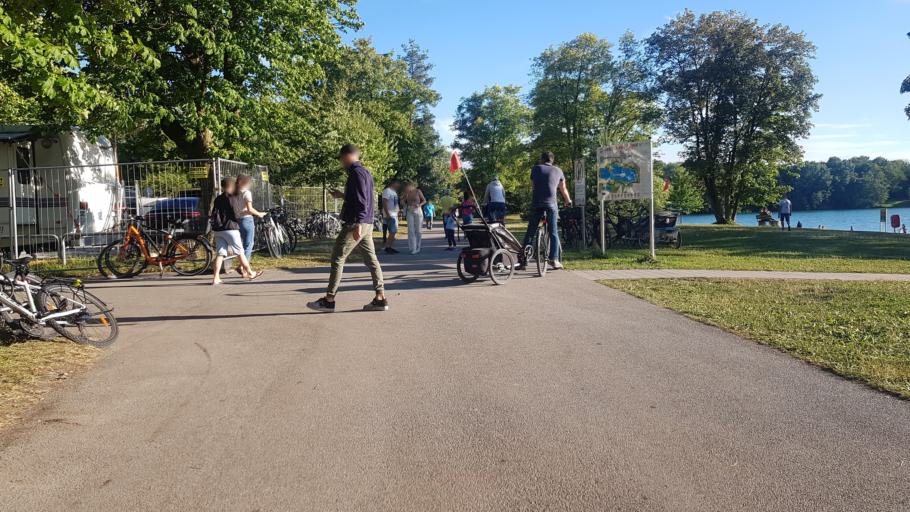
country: DE
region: Bavaria
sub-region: Upper Bavaria
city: Karlsfeld
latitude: 48.2359
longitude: 11.4708
